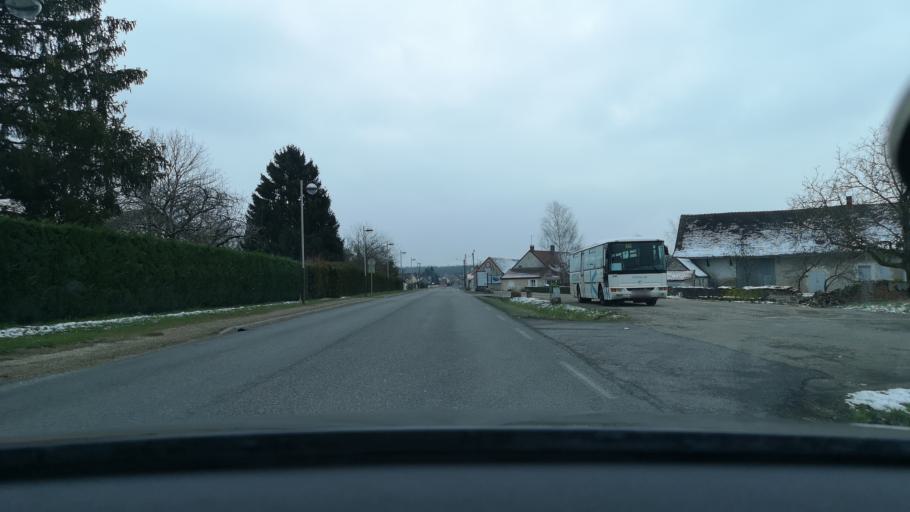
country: FR
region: Bourgogne
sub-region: Departement de Saone-et-Loire
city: Saint-Marcel
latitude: 46.7837
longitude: 4.9251
